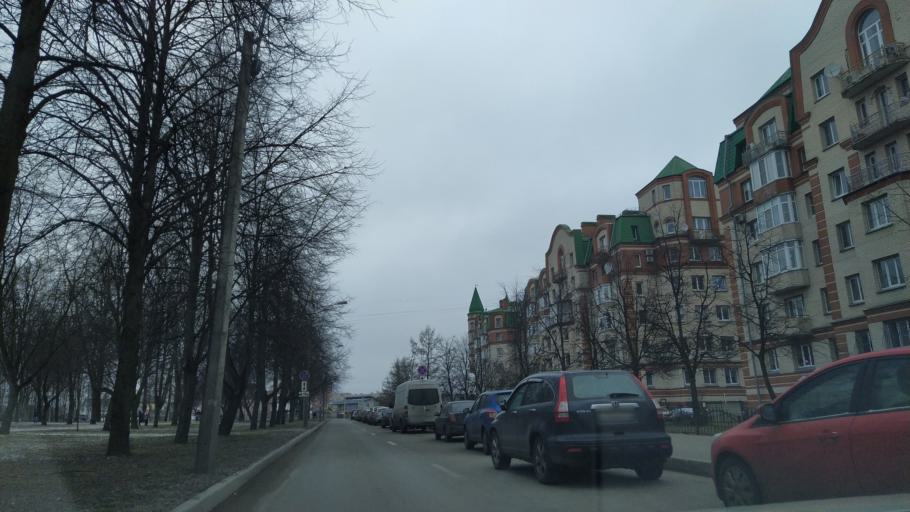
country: RU
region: St.-Petersburg
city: Pushkin
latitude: 59.7330
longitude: 30.4134
